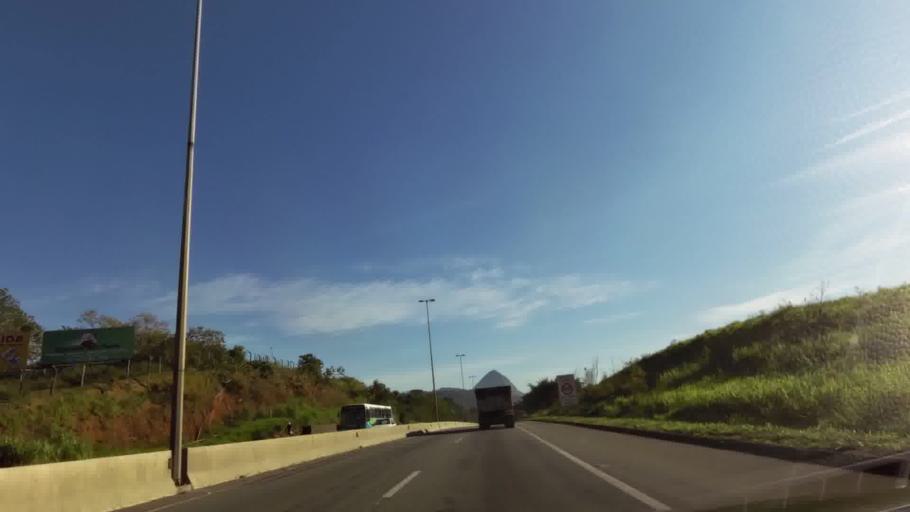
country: BR
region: Espirito Santo
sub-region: Viana
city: Viana
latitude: -20.3699
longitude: -40.4439
